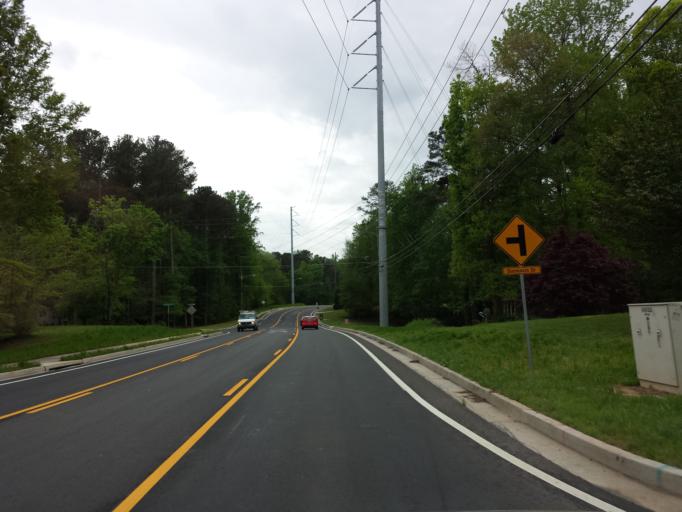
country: US
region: Georgia
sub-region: Cherokee County
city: Woodstock
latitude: 34.0601
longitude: -84.5642
